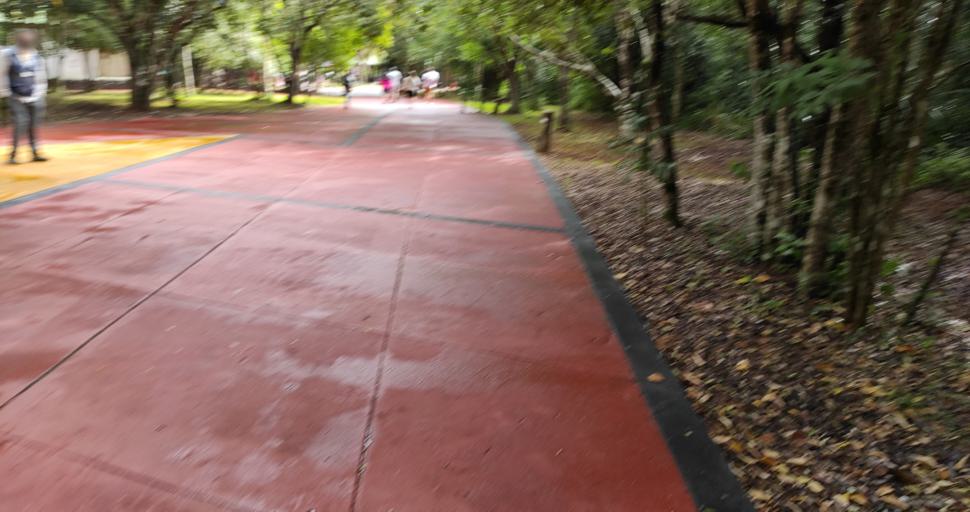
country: AR
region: Misiones
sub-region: Departamento de Iguazu
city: Puerto Iguazu
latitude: -25.6817
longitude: -54.4537
